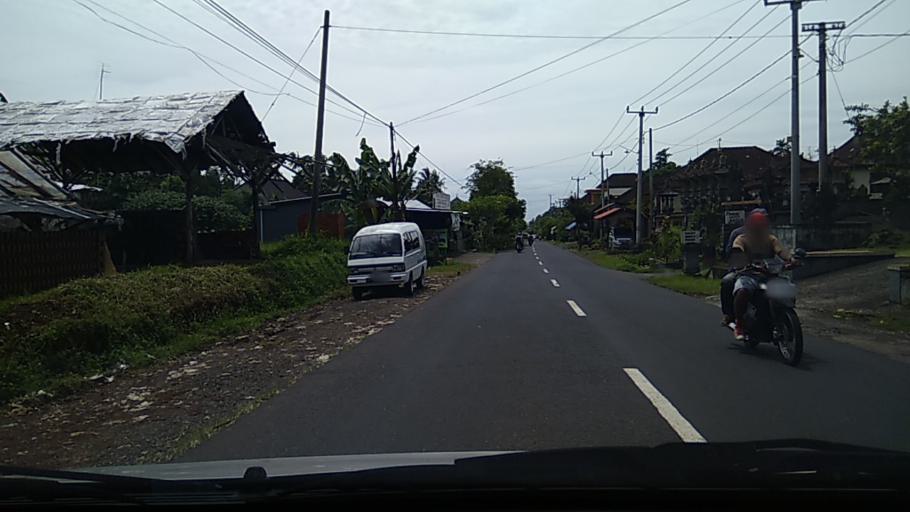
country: ID
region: Bali
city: Wanasari Baleran
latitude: -8.4717
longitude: 115.1370
